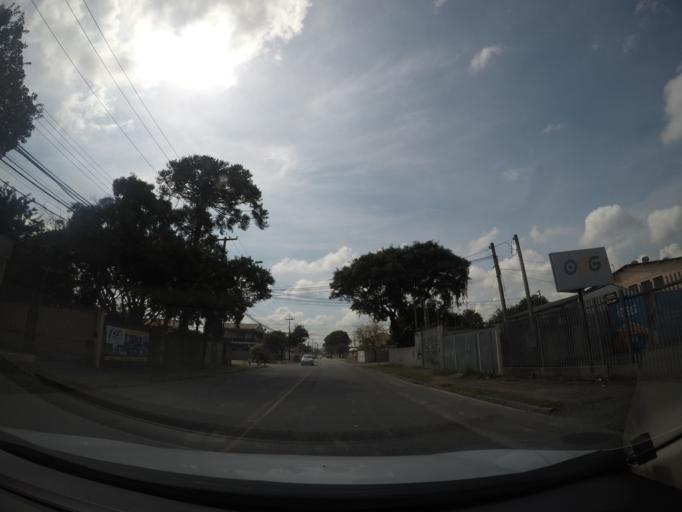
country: BR
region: Parana
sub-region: Curitiba
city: Curitiba
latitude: -25.4745
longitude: -49.2635
